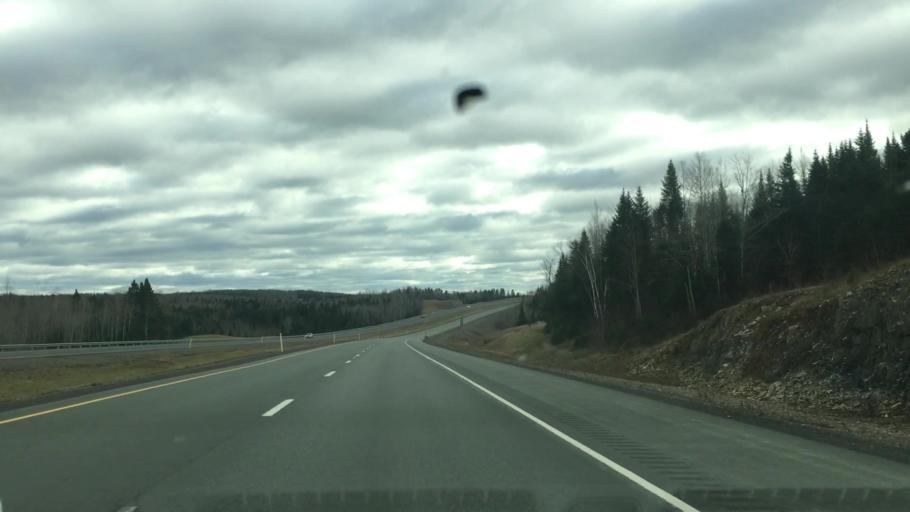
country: CA
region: New Brunswick
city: Florenceville-Bristol
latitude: 46.5427
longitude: -67.7166
